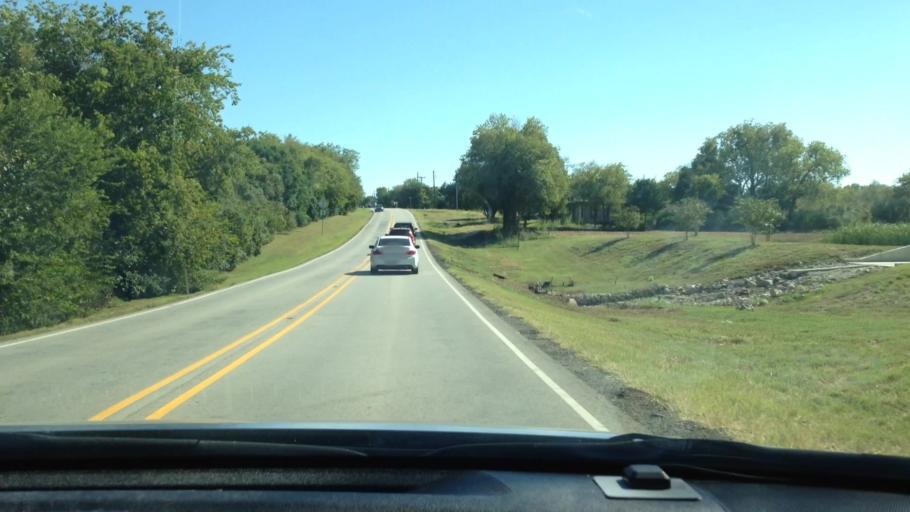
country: US
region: Texas
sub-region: Collin County
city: Lucas
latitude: 33.0731
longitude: -96.5716
